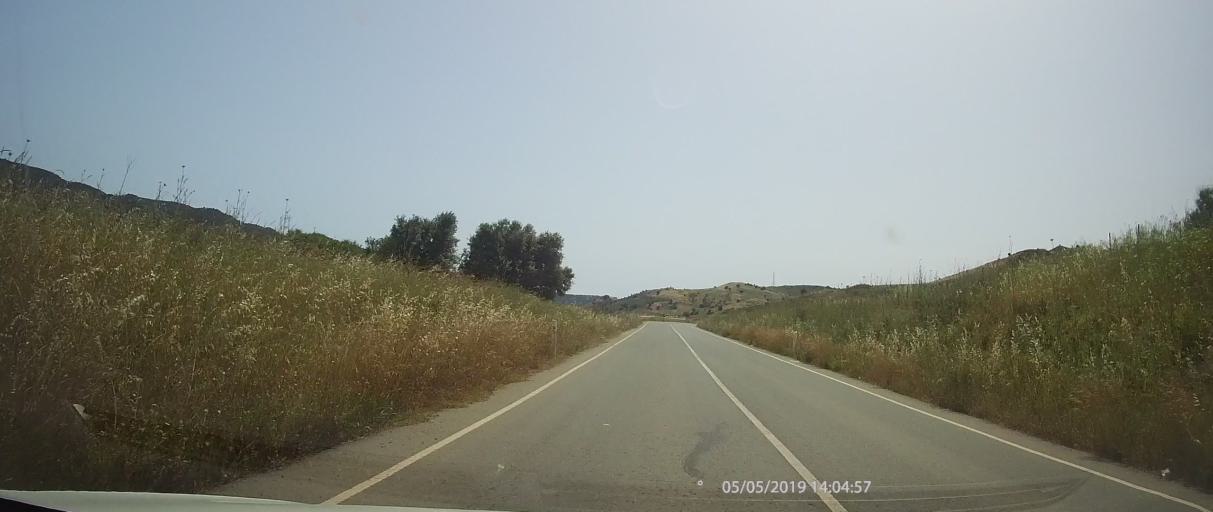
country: CY
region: Limassol
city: Pissouri
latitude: 34.7576
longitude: 32.6189
